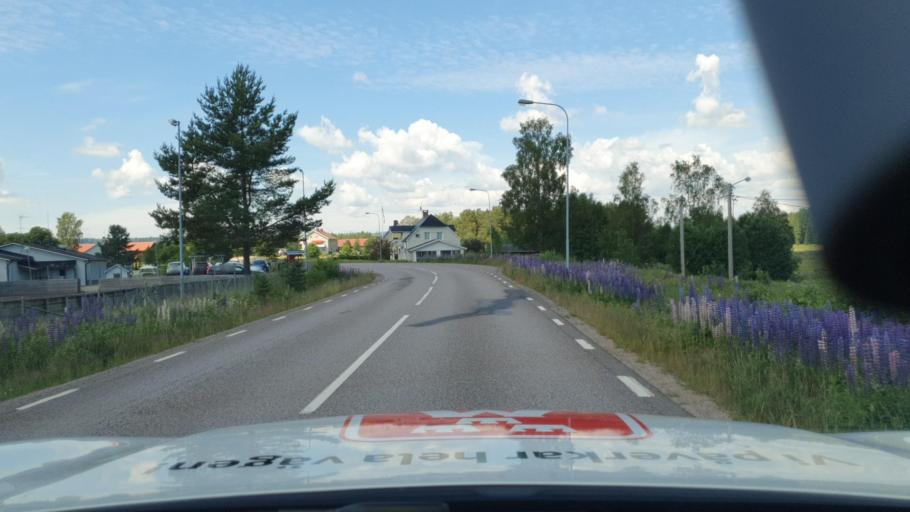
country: SE
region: Vaermland
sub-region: Torsby Kommun
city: Torsby
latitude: 60.3419
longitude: 12.9846
